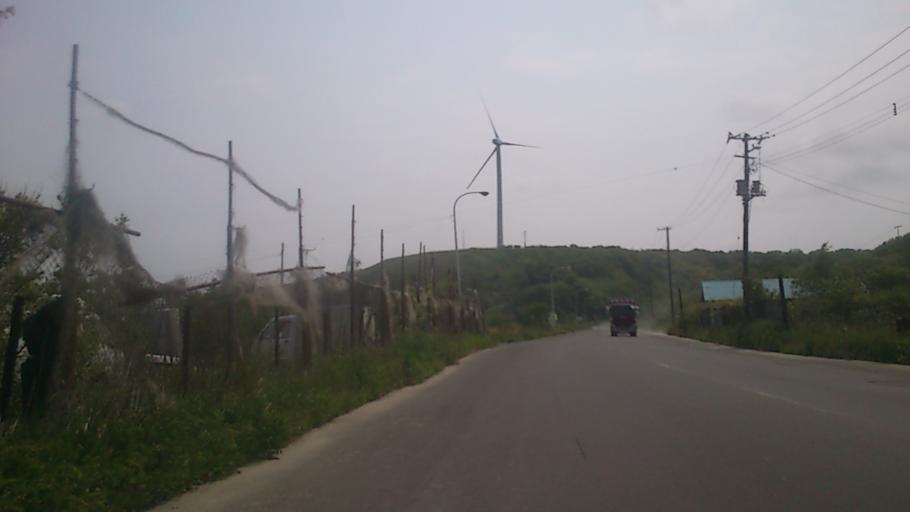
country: JP
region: Hokkaido
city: Nemuro
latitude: 43.2812
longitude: 145.5641
